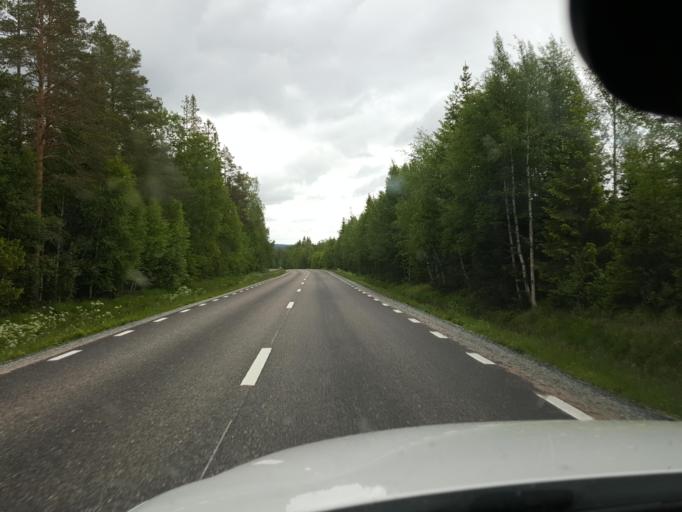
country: SE
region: Gaevleborg
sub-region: Ljusdals Kommun
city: Farila
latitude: 61.7575
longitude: 15.4115
